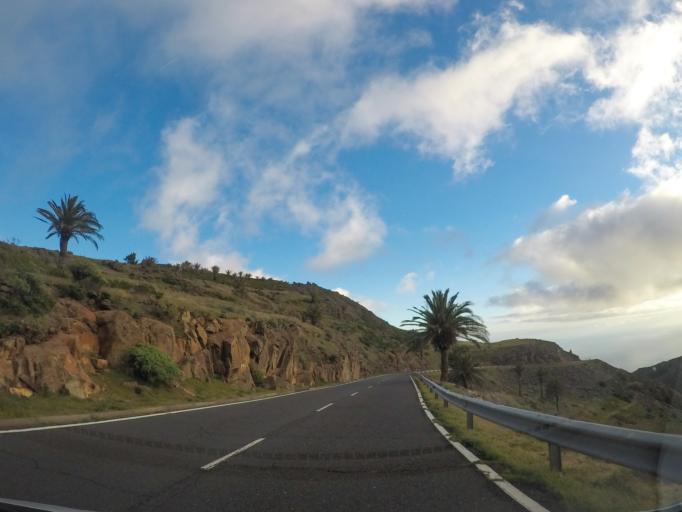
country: ES
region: Canary Islands
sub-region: Provincia de Santa Cruz de Tenerife
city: Alajero
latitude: 28.0848
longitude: -17.2453
